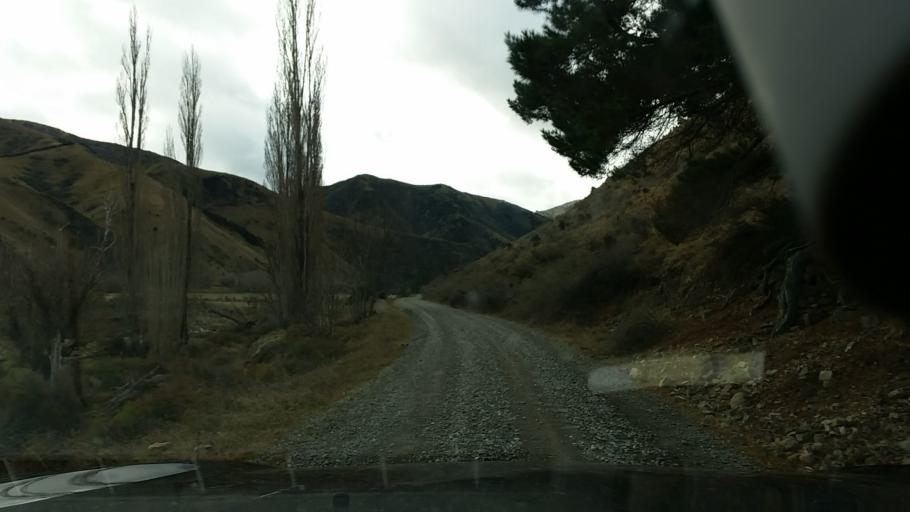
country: NZ
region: Tasman
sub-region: Tasman District
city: Brightwater
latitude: -41.7436
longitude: 173.4142
